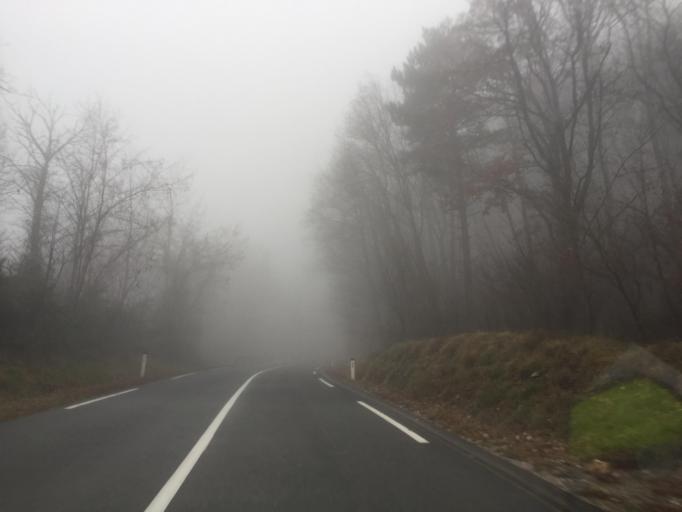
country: SI
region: Ajdovscina
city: Lokavec
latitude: 45.9304
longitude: 13.8885
